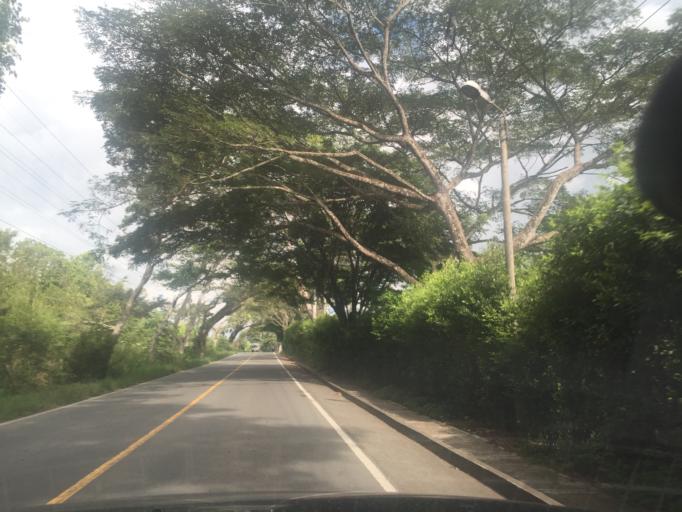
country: CO
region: Valle del Cauca
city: Caicedonia
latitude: 4.3416
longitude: -75.8380
